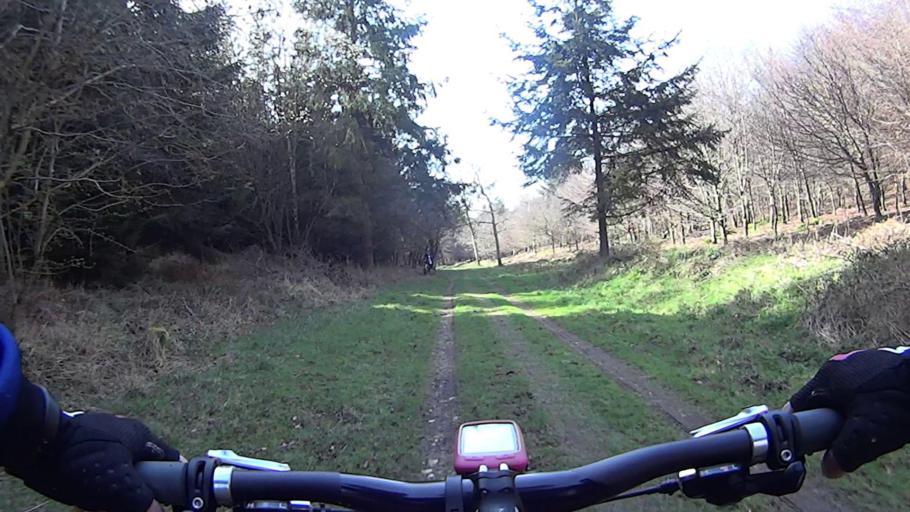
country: GB
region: England
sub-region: West Sussex
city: Midhurst
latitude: 50.9306
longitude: -0.7192
